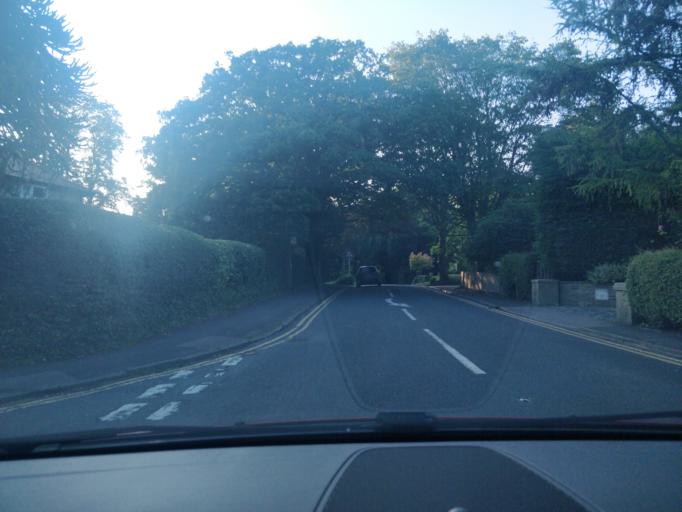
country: GB
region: England
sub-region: Lancashire
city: Parbold
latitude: 53.5935
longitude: -2.7649
